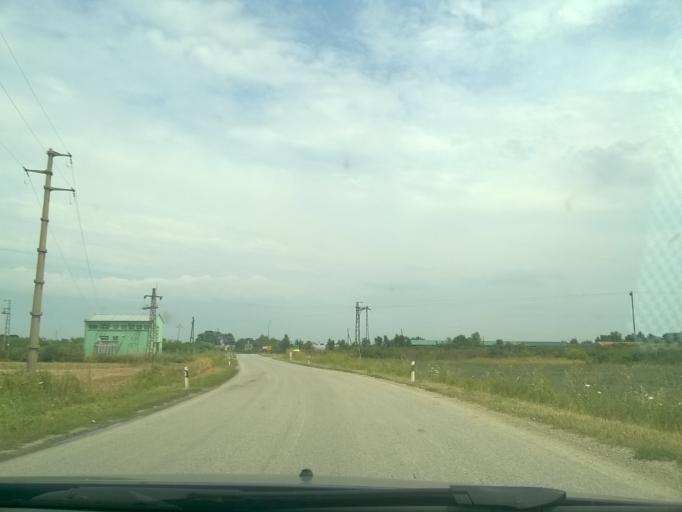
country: RS
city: Boka
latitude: 45.3456
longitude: 20.8230
